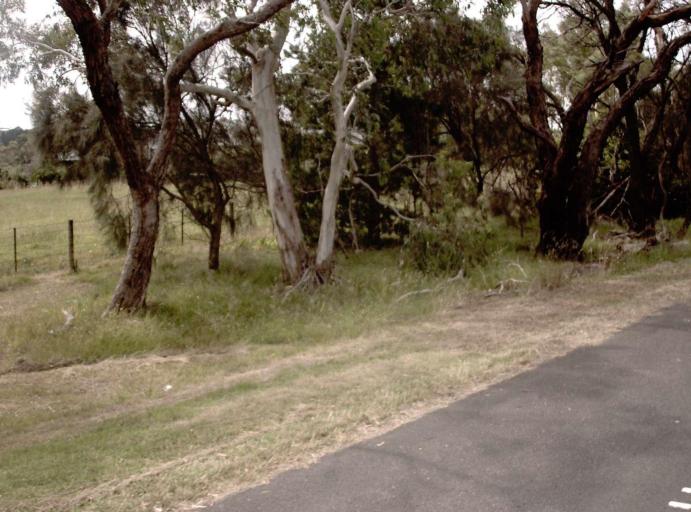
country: AU
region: Victoria
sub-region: Mornington Peninsula
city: Moorooduc
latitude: -38.2477
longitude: 145.0827
